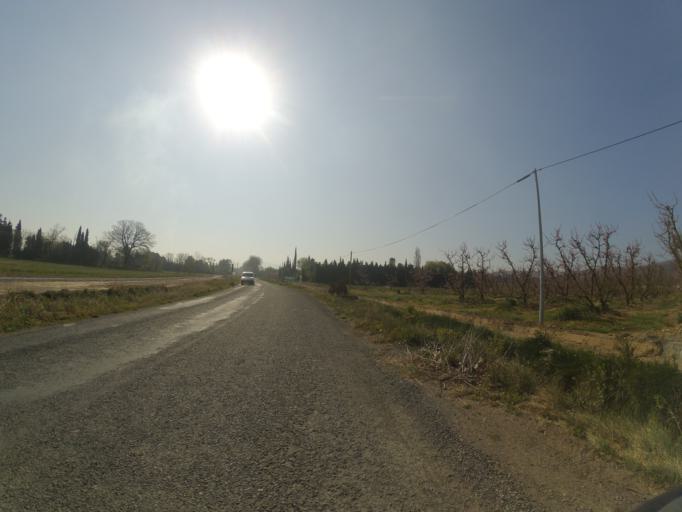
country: FR
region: Languedoc-Roussillon
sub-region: Departement des Pyrenees-Orientales
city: Thuir
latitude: 42.6456
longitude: 2.7381
